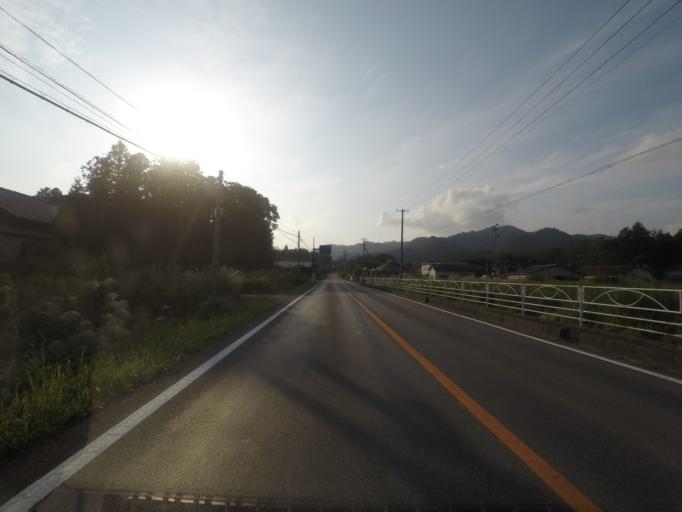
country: JP
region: Fukushima
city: Namie
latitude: 37.5066
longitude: 140.9380
